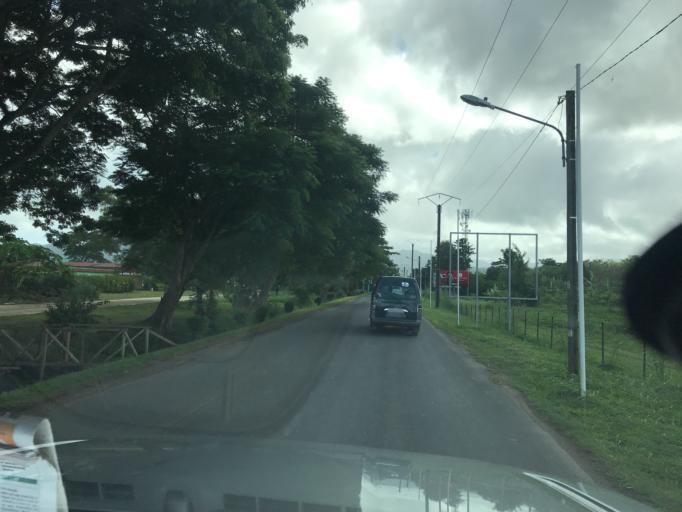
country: VU
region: Shefa
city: Port-Vila
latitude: -17.7046
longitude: 168.3181
